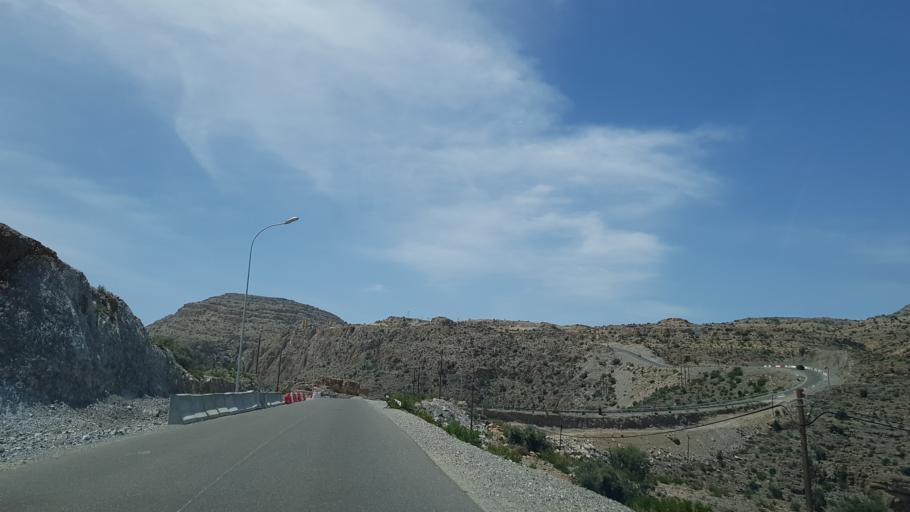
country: OM
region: Muhafazat ad Dakhiliyah
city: Izki
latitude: 23.0960
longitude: 57.6754
